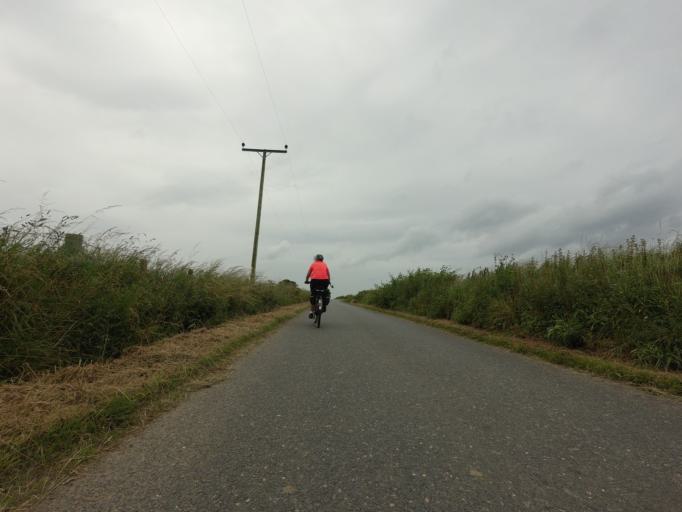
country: GB
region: Scotland
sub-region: Aberdeenshire
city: Portsoy
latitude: 57.6627
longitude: -2.7517
